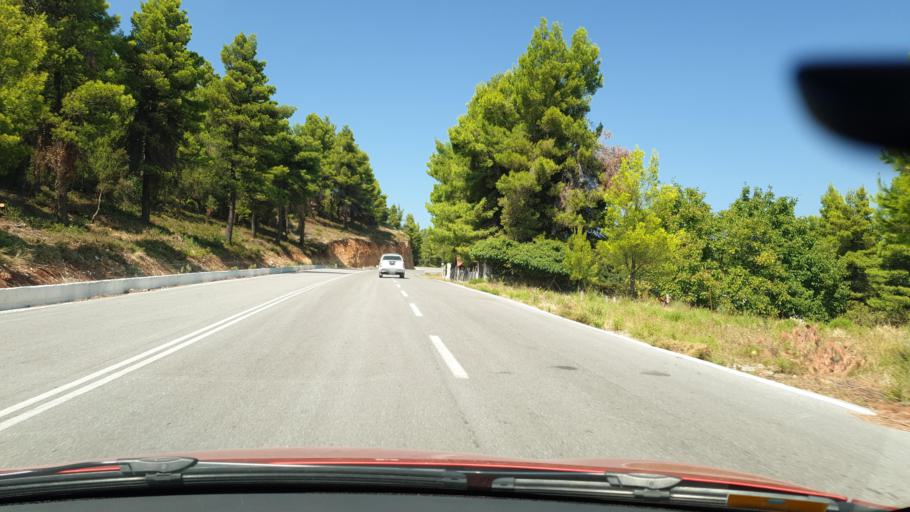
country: GR
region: Central Greece
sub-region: Nomos Evvoias
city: Politika
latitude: 38.6366
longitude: 23.5653
